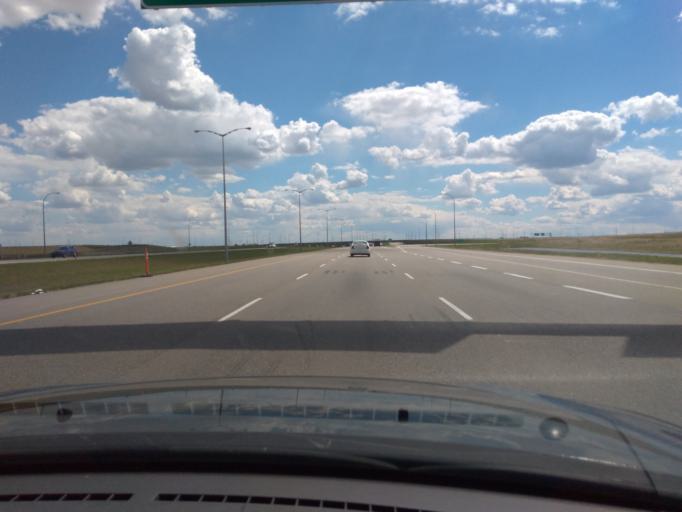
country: CA
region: Alberta
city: Chestermere
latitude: 51.0230
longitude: -113.9213
